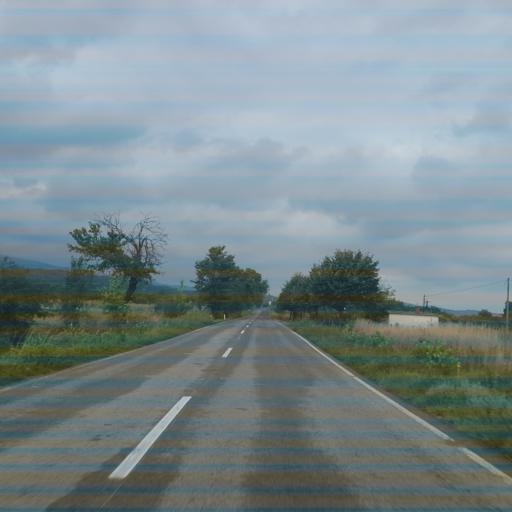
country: RS
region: Central Serbia
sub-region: Nisavski Okrug
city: Aleksinac
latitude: 43.5899
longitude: 21.6424
